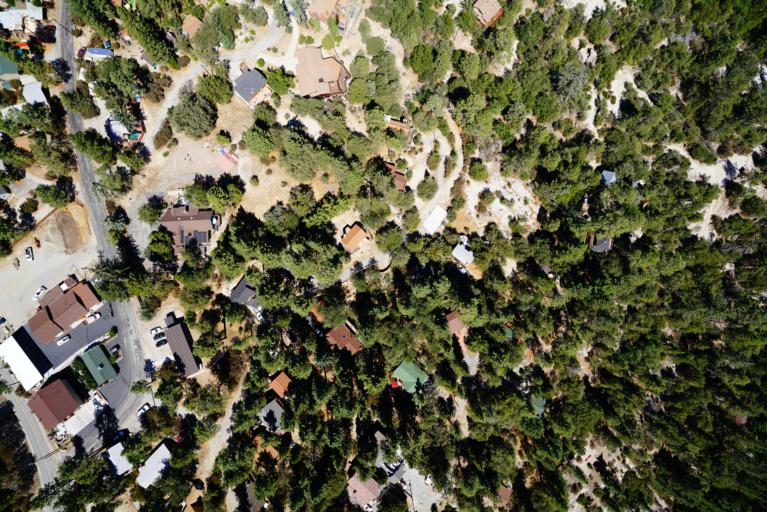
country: US
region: California
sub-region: Riverside County
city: Idyllwild-Pine Cove
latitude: 33.7608
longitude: -116.7360
